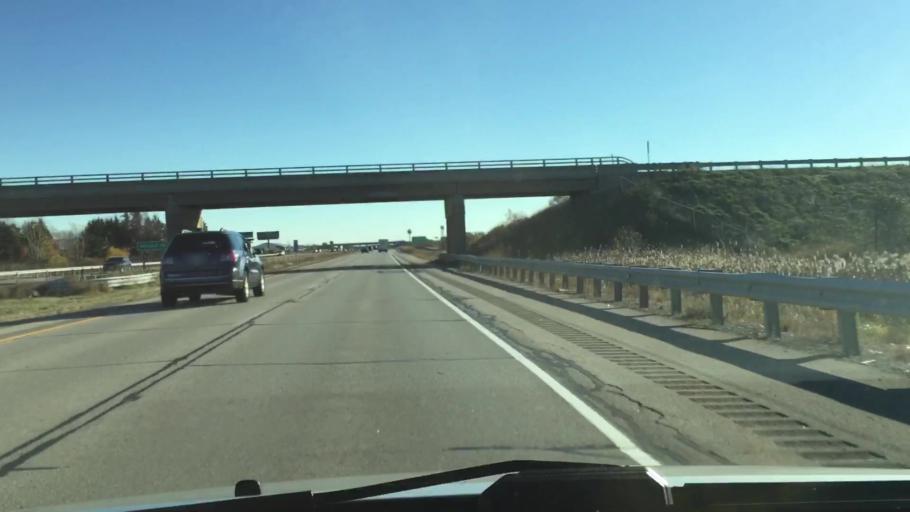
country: US
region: Wisconsin
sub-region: Outagamie County
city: Little Chute
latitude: 44.2978
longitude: -88.3338
